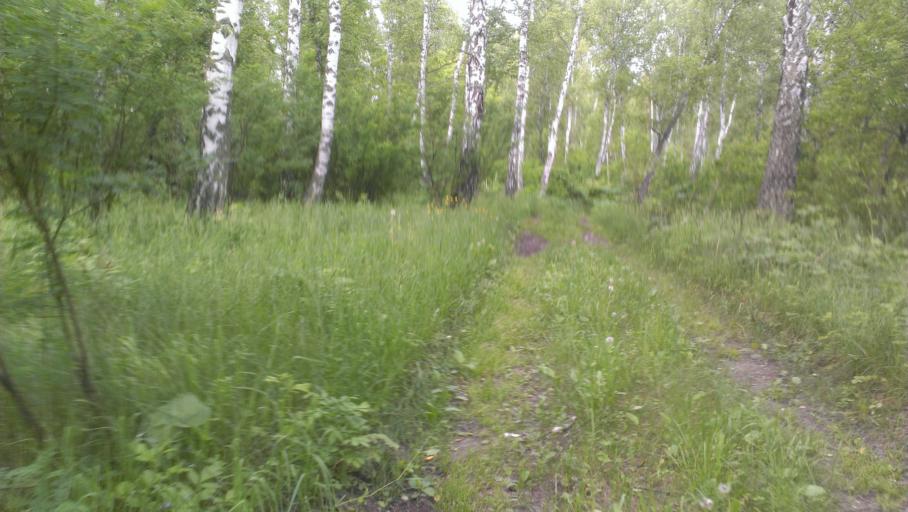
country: RU
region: Altai Krai
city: Sannikovo
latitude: 53.3430
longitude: 84.0602
